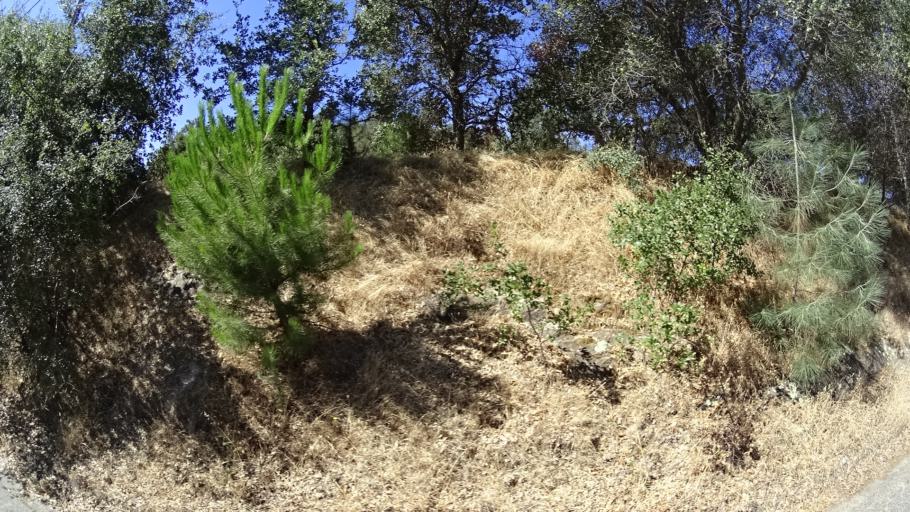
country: US
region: California
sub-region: Calaveras County
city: Rancho Calaveras
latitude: 38.1644
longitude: -120.8563
